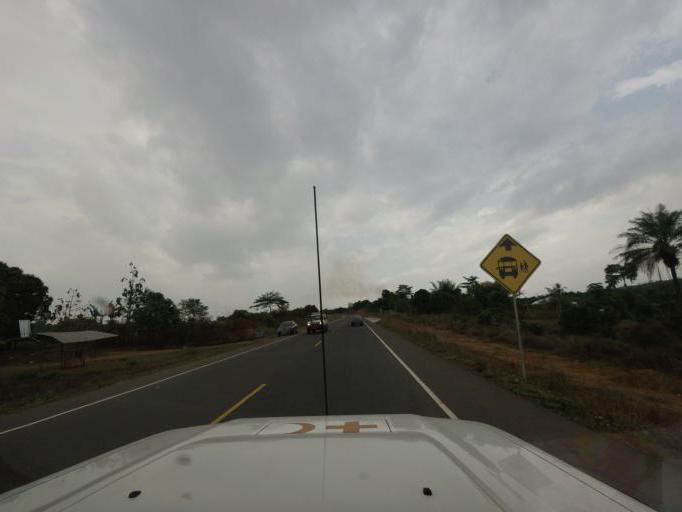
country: LR
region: Montserrado
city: Bensonville City
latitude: 6.4021
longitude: -10.5660
